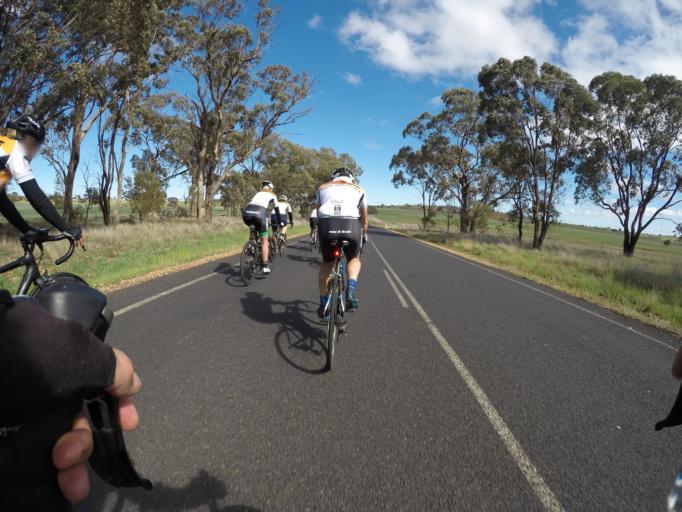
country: AU
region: New South Wales
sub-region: Wellington
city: Wellington
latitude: -32.7497
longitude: 148.6122
